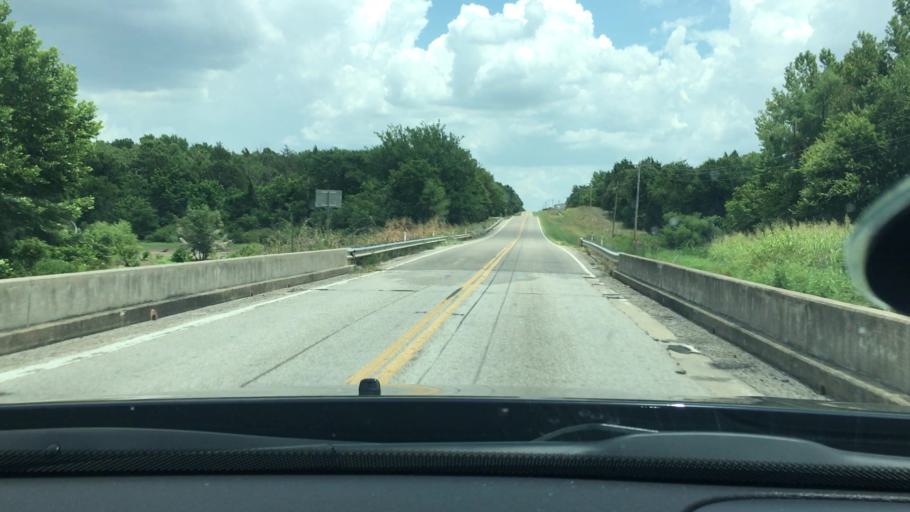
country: US
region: Oklahoma
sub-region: Love County
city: Marietta
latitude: 33.9839
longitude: -96.9755
